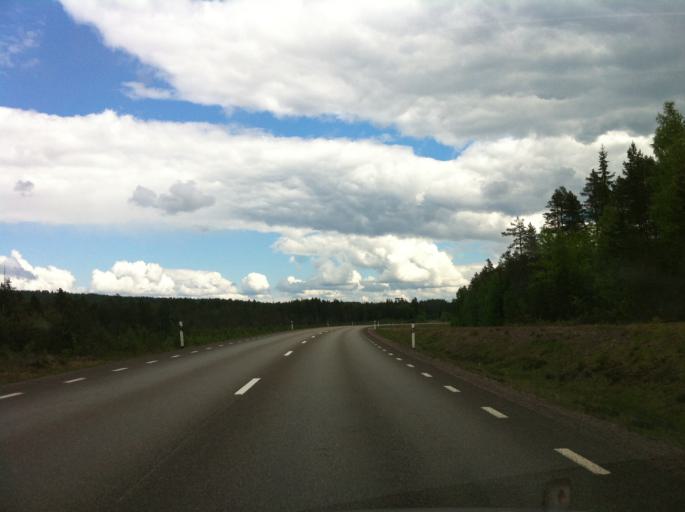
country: SE
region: Dalarna
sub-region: Malung-Saelens kommun
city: Malung
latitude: 60.6468
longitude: 13.6320
